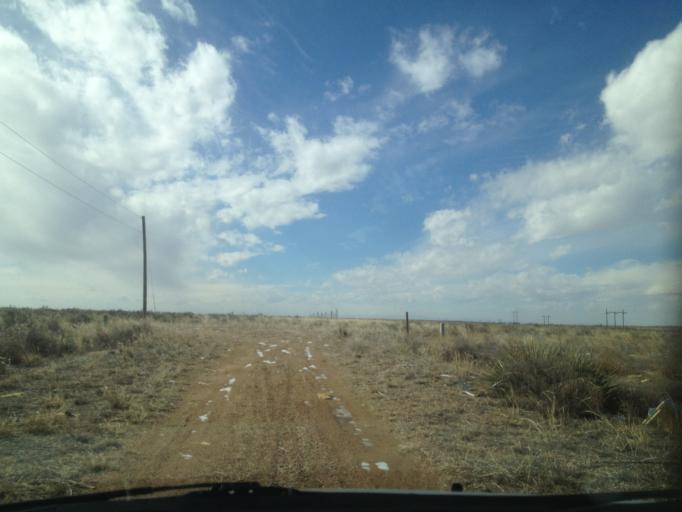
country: US
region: Colorado
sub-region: Weld County
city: Keenesburg
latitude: 40.2821
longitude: -104.2620
